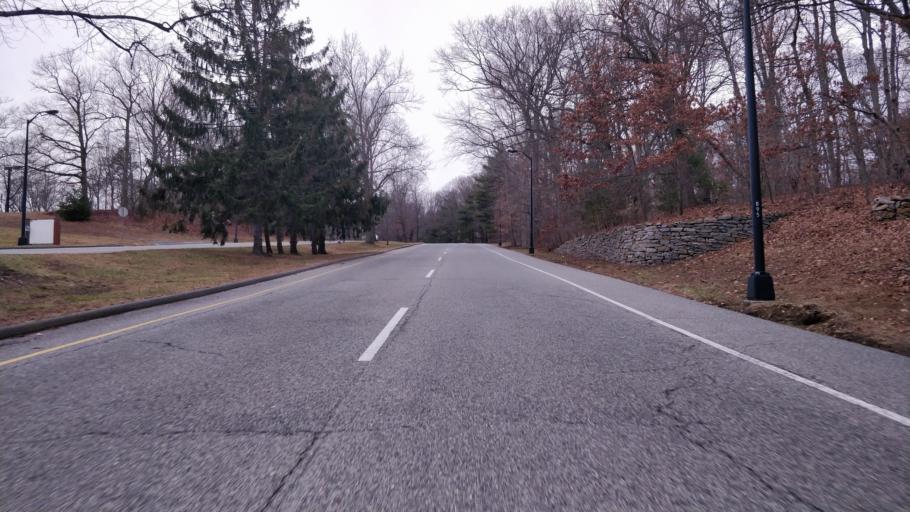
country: US
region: New York
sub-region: Nassau County
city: Brookville
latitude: 40.7983
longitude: -73.5674
